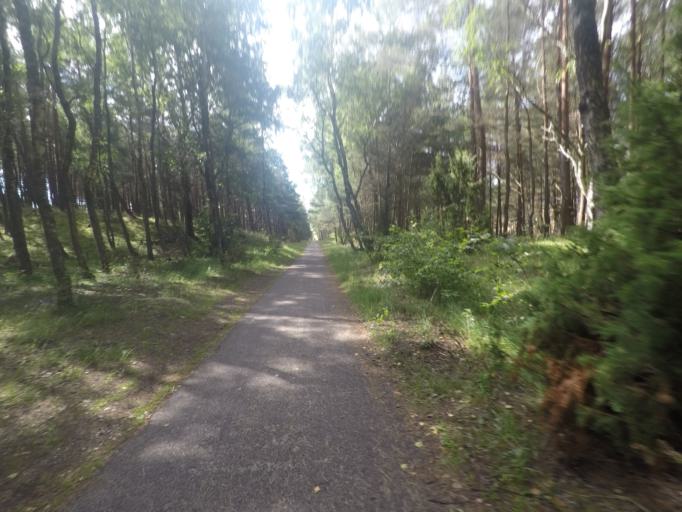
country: LT
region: Klaipedos apskritis
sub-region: Klaipeda
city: Klaipeda
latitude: 55.6462
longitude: 21.1083
